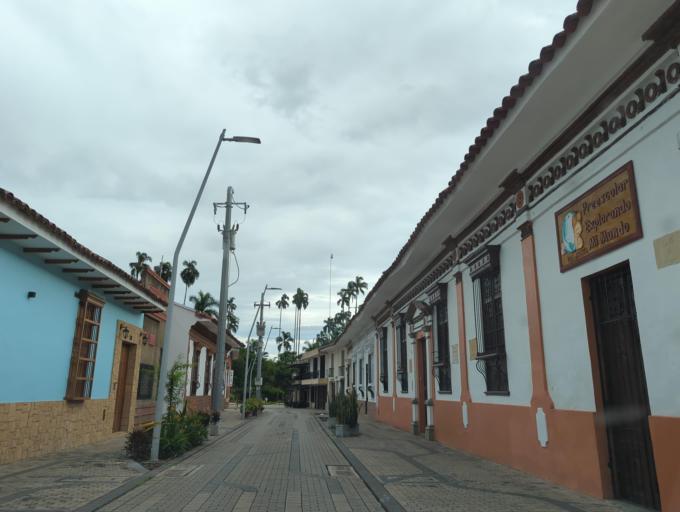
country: CO
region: Valle del Cauca
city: Buga
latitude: 3.8957
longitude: -76.3021
